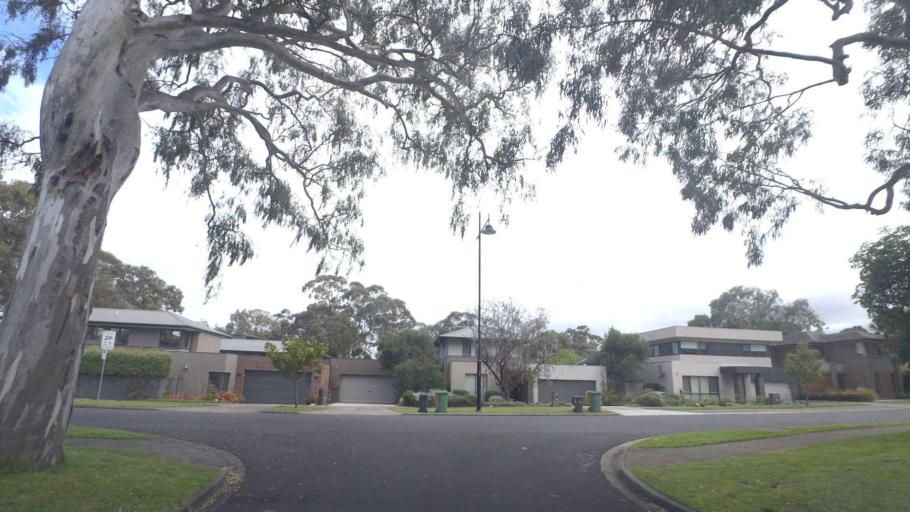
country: AU
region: Victoria
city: Macleod
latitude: -37.7176
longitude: 145.0639
